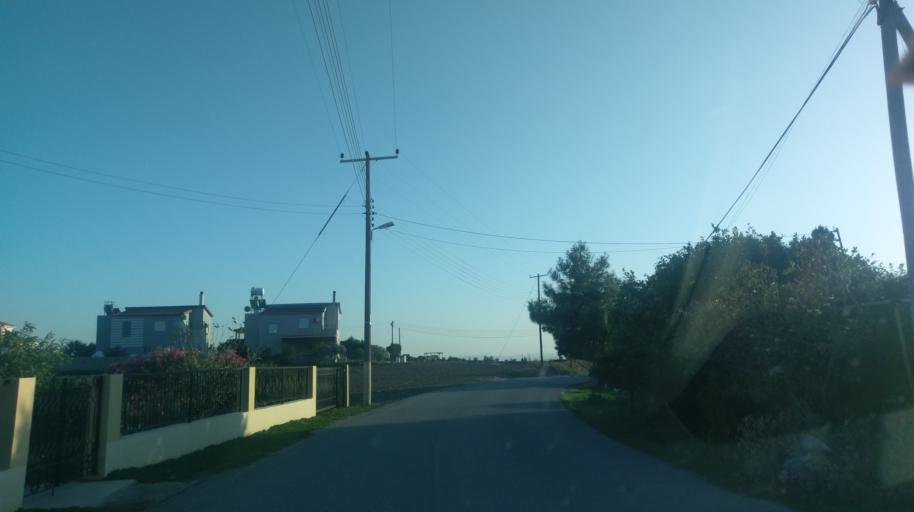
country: CY
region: Ammochostos
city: Lefkonoiko
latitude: 35.2550
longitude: 33.5497
